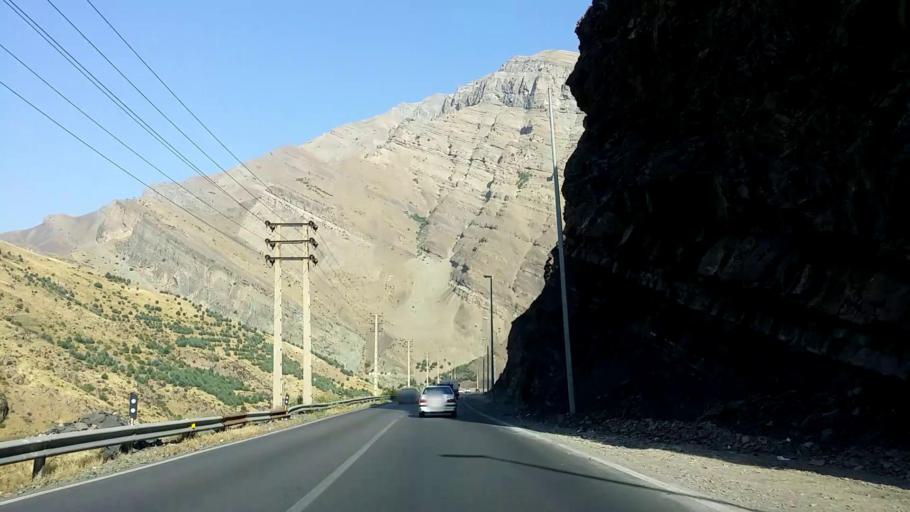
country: IR
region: Alborz
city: Karaj
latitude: 36.0108
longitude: 51.1358
